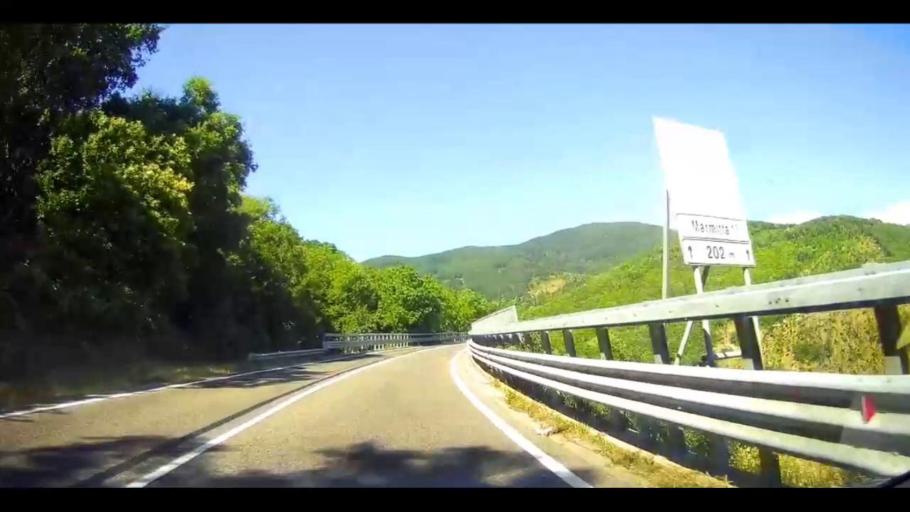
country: IT
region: Calabria
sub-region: Provincia di Cosenza
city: Spezzano Piccolo
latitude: 39.2903
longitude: 16.3490
